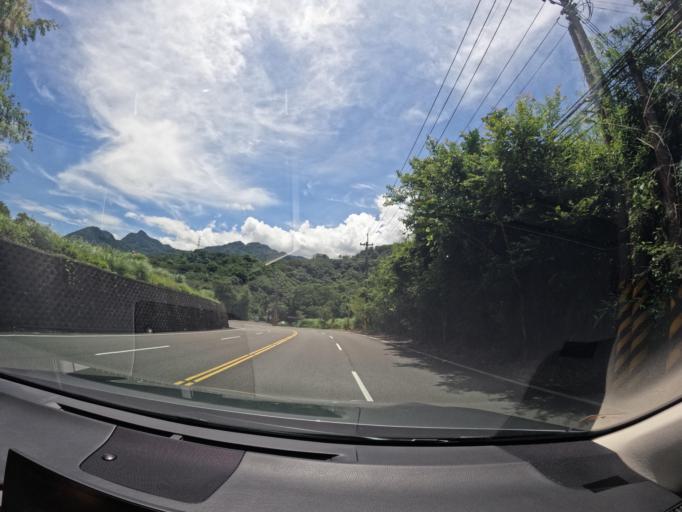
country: TW
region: Taiwan
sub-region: Miaoli
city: Miaoli
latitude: 24.5297
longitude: 120.9160
